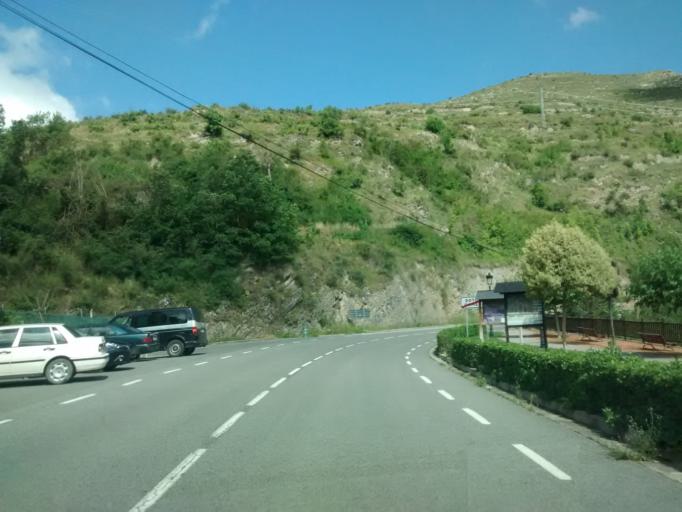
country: ES
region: La Rioja
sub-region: Provincia de La Rioja
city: Soto en Cameros
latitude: 42.2873
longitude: -2.4279
